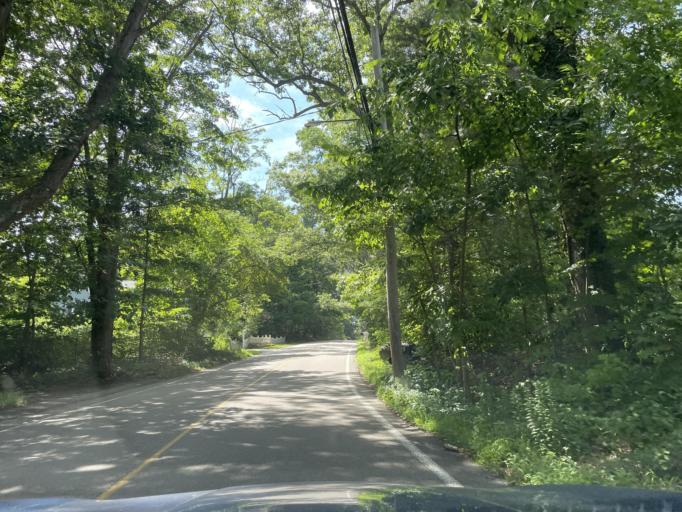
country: US
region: Massachusetts
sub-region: Middlesex County
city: Sherborn
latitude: 42.2376
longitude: -71.3906
